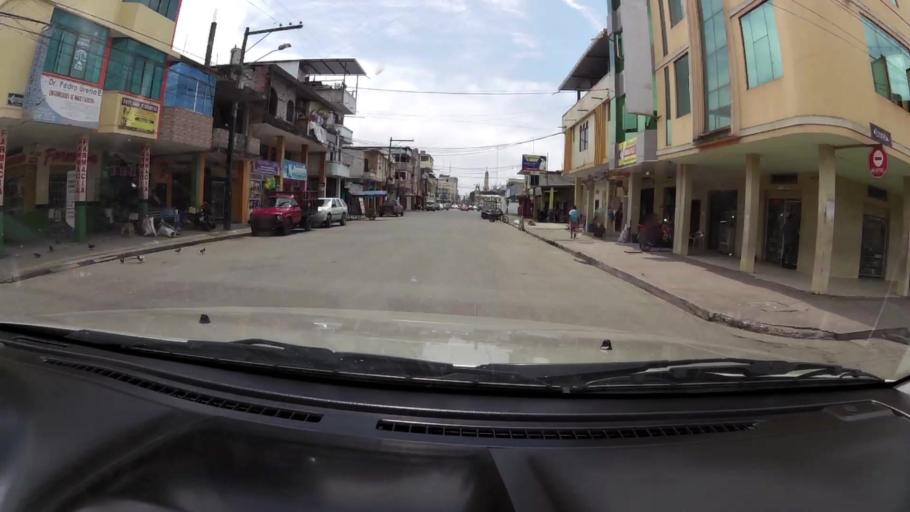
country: EC
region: El Oro
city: Pasaje
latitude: -3.2439
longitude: -79.8294
